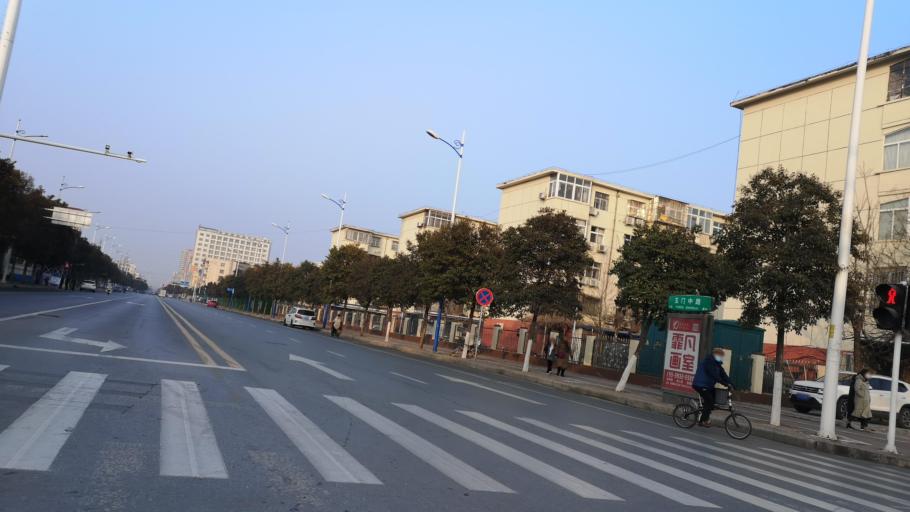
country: CN
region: Henan Sheng
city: Zhongyuanlu
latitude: 35.7633
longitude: 115.0623
